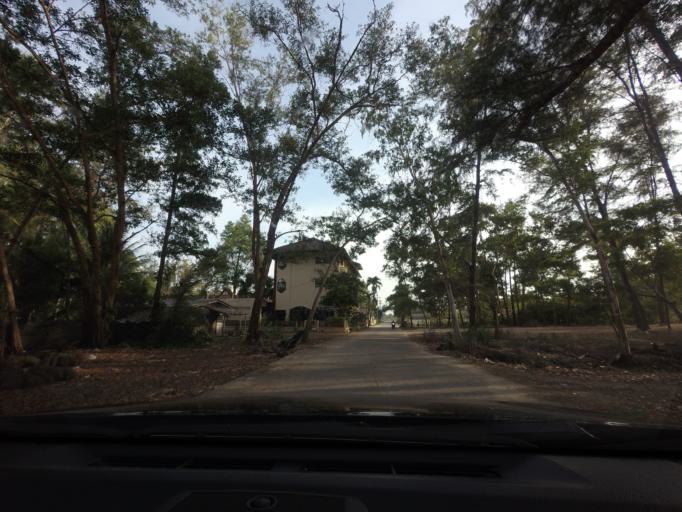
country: TH
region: Narathiwat
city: Narathiwat
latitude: 6.4277
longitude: 101.8539
